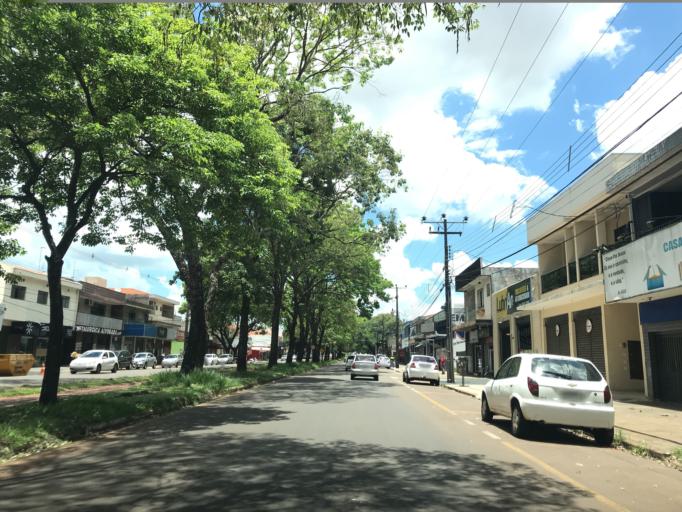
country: BR
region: Parana
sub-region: Maringa
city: Maringa
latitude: -23.3962
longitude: -51.9185
